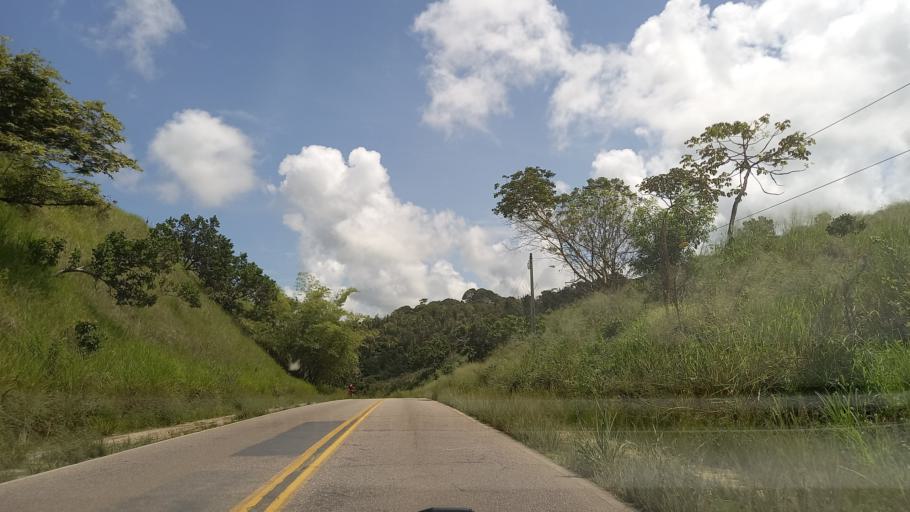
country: BR
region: Pernambuco
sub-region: Barreiros
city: Barreiros
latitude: -8.7668
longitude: -35.1695
